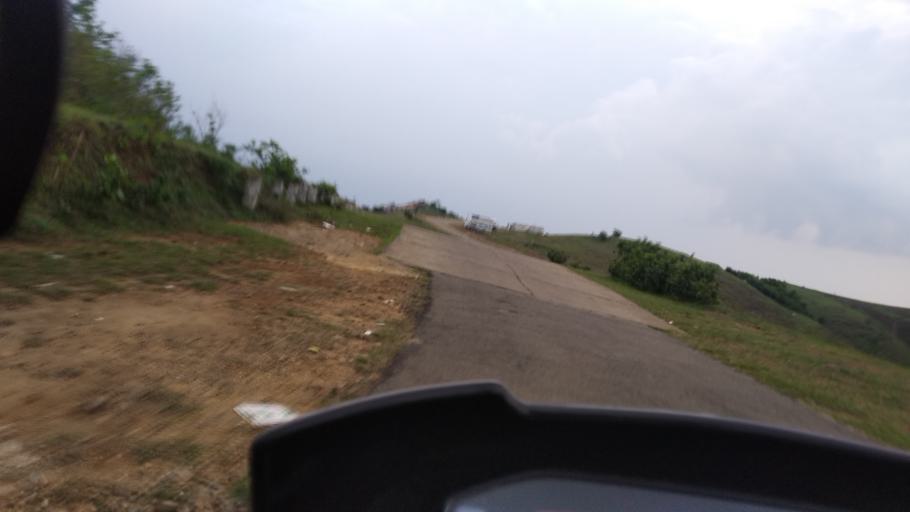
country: IN
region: Tamil Nadu
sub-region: Theni
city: Gudalur
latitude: 9.5490
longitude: 77.0334
